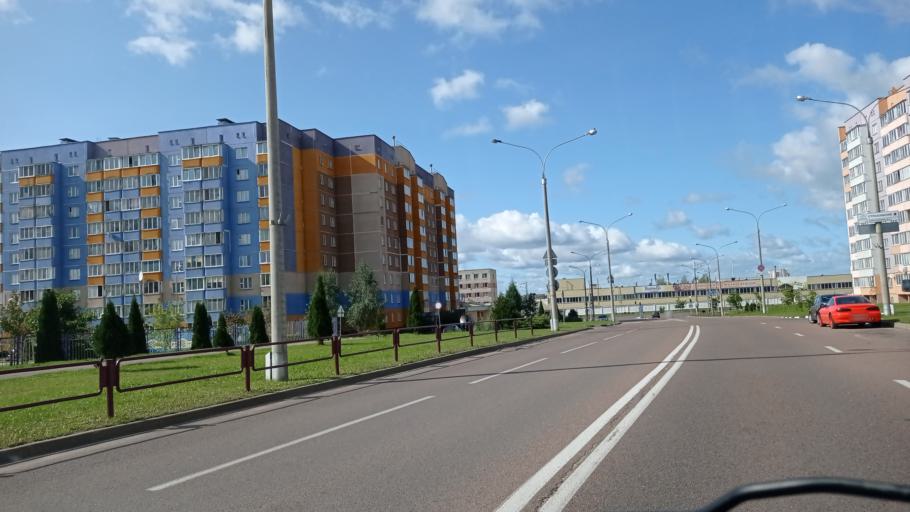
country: BY
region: Vitebsk
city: Vitebsk
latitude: 55.1698
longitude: 30.2601
